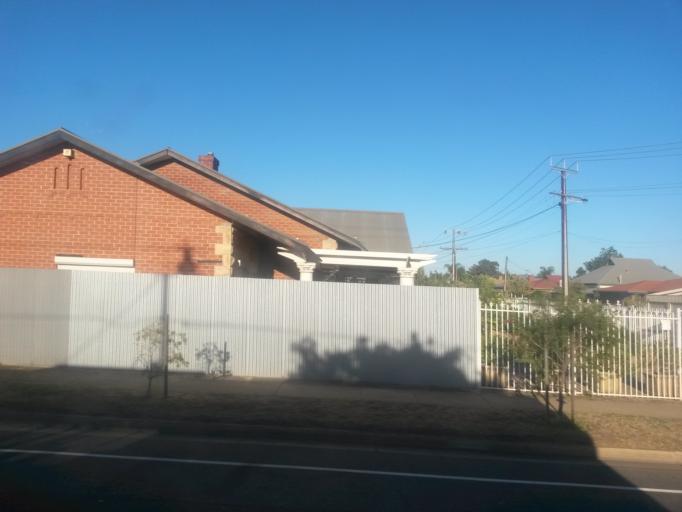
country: AU
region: South Australia
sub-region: Port Adelaide Enfield
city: Alberton
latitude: -34.8589
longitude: 138.5292
